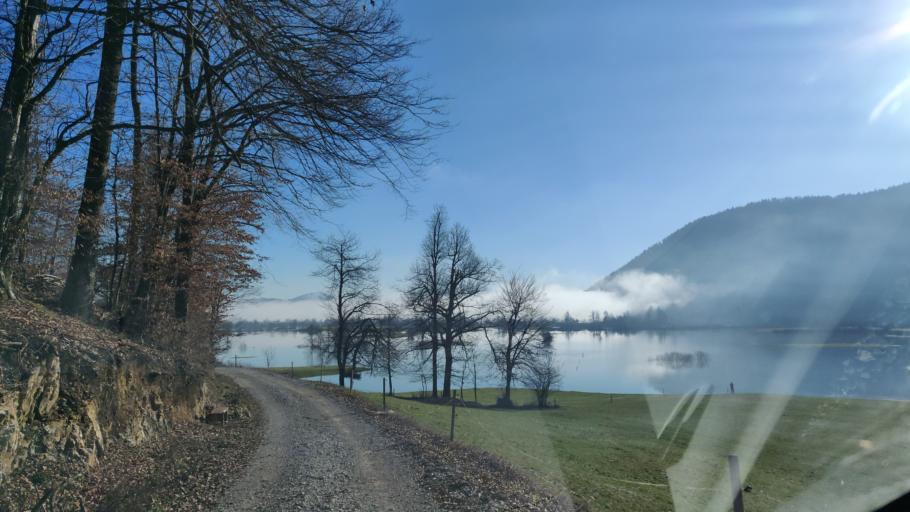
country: SI
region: Logatec
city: Logatec
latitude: 45.8691
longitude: 14.2240
